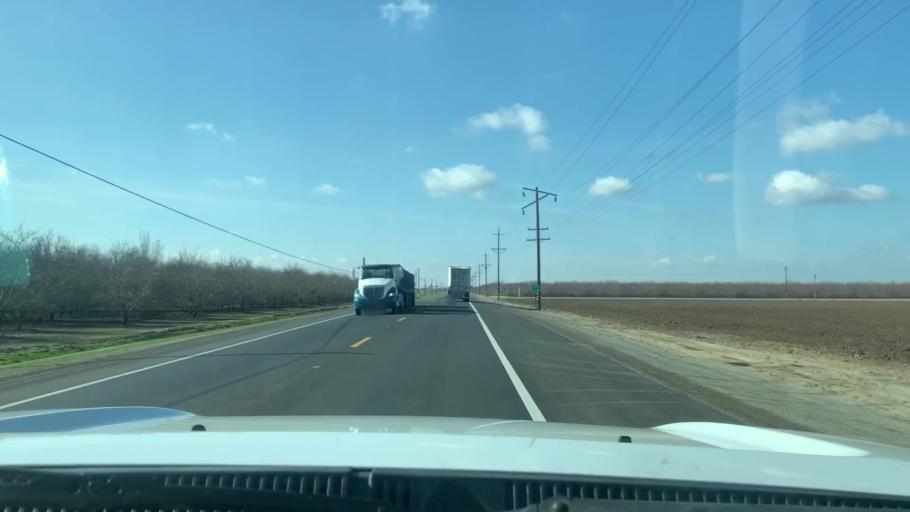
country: US
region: California
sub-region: Kern County
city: Wasco
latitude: 35.6017
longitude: -119.3095
